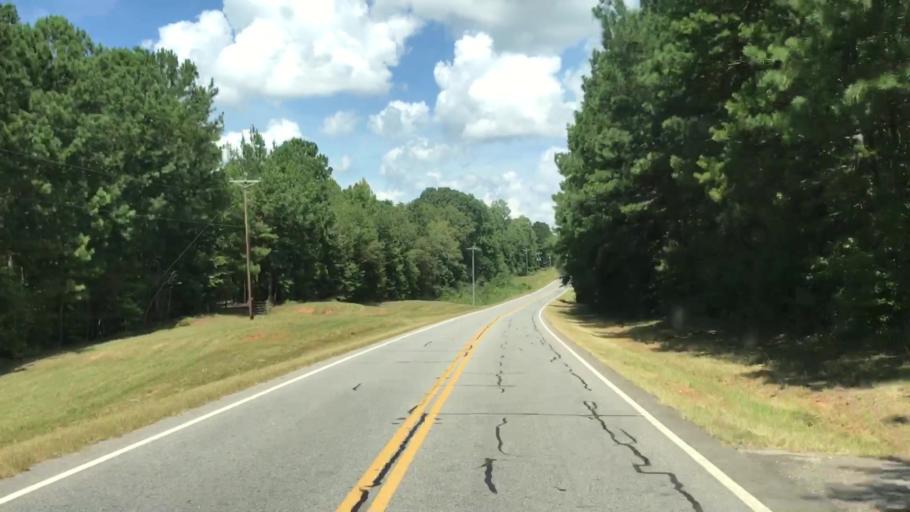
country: US
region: Georgia
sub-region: Oconee County
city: Watkinsville
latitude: 33.7617
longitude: -83.3088
